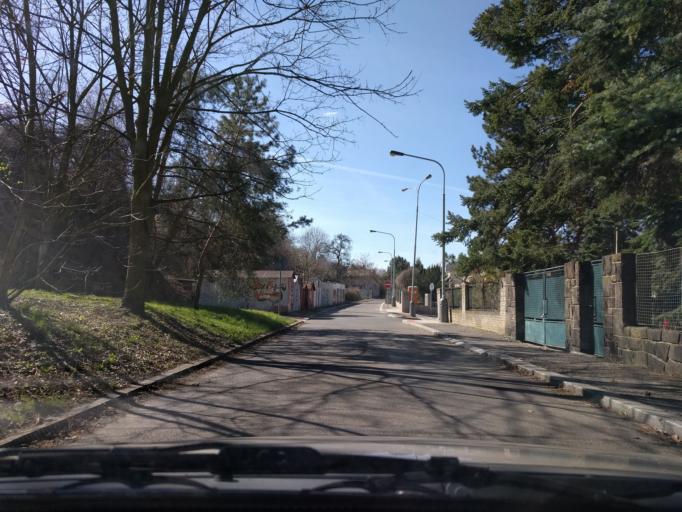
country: CZ
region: Praha
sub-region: Praha 1
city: Mala Strana
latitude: 50.0980
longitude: 14.3806
